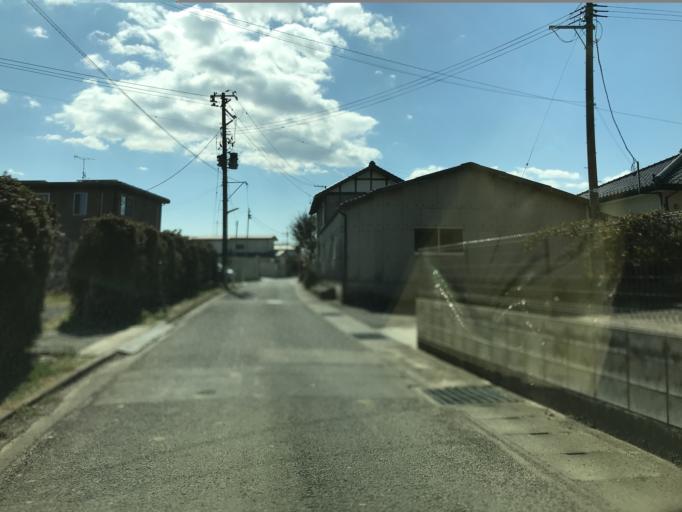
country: JP
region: Fukushima
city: Fukushima-shi
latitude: 37.7422
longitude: 140.4127
